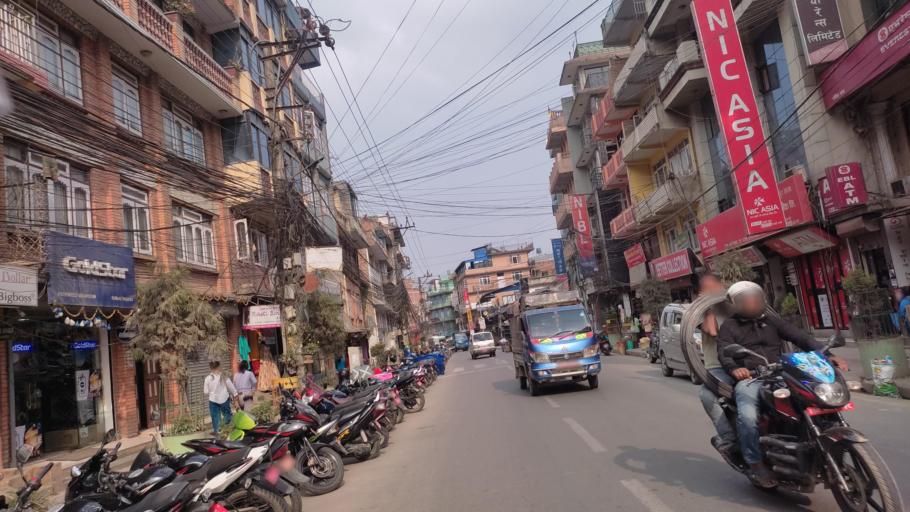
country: NP
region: Central Region
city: Kirtipur
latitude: 27.6747
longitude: 85.2788
